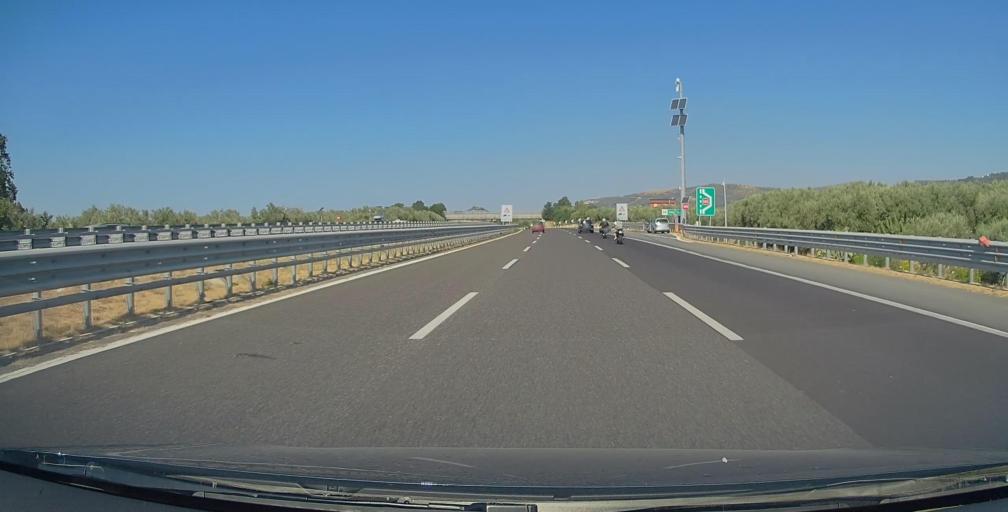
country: IT
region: Campania
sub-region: Provincia di Salerno
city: Quadrivio
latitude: 40.6098
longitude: 15.0845
